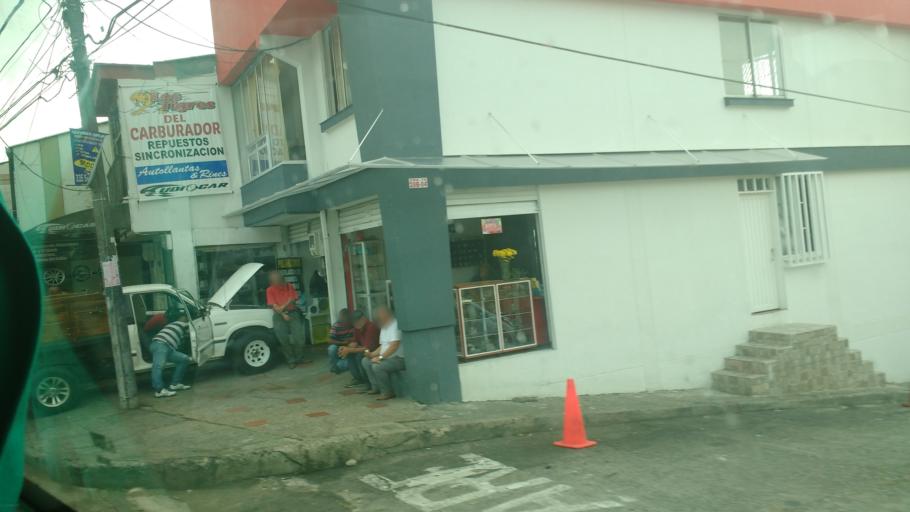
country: CO
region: Risaralda
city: Pereira
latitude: 4.8115
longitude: -75.7026
